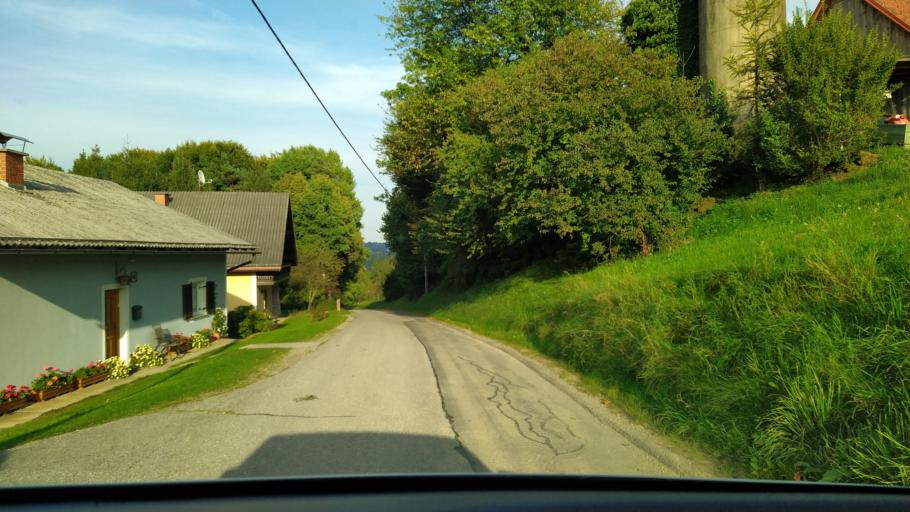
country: AT
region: Styria
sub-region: Politischer Bezirk Leibnitz
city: Arnfels
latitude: 46.6699
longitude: 15.3875
